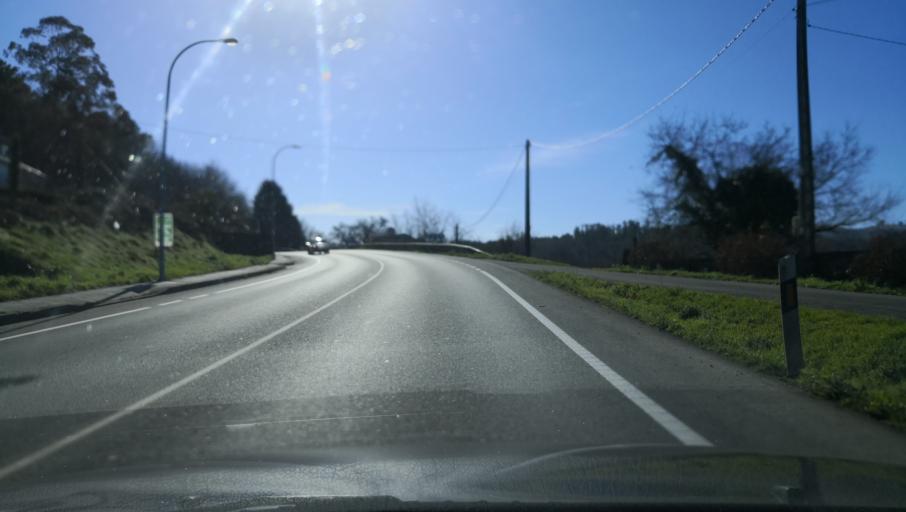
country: ES
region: Galicia
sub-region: Provincia de Pontevedra
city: Silleda
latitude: 42.7005
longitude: -8.2548
